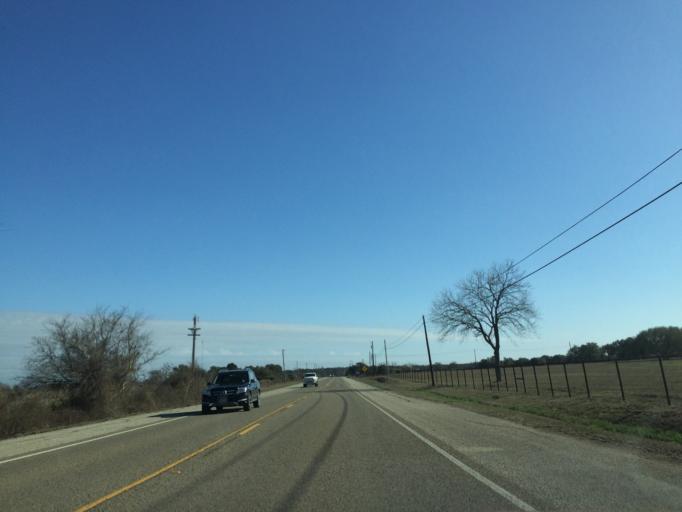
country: US
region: Texas
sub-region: Williamson County
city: Florence
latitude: 30.7777
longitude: -97.8506
